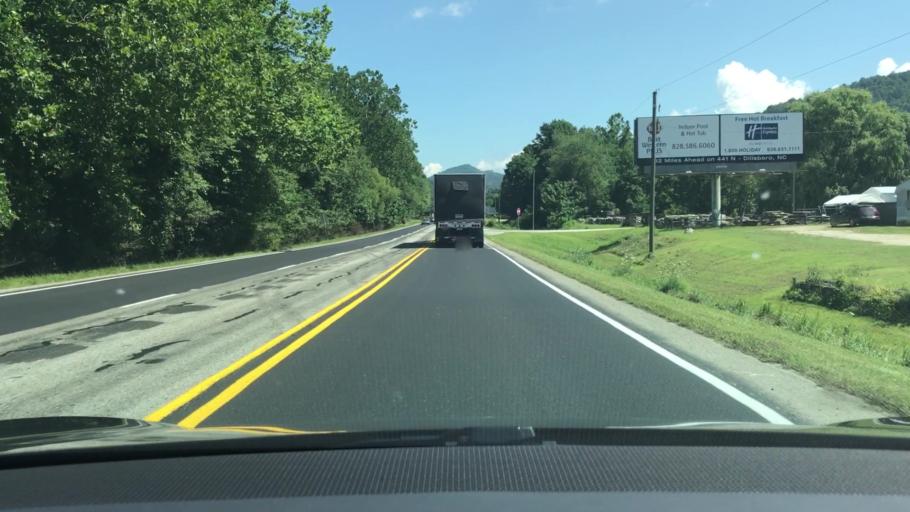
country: US
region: Georgia
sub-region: Rabun County
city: Mountain City
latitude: 34.9902
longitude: -83.3833
